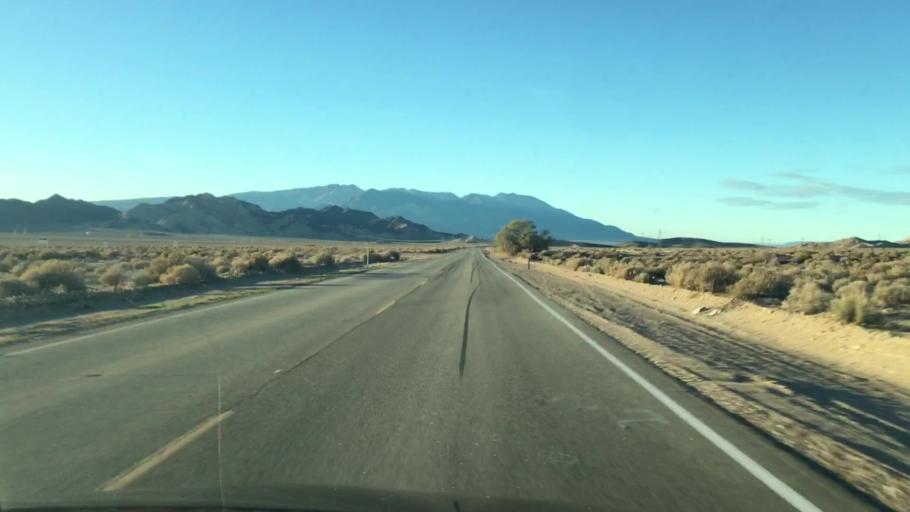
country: US
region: California
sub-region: San Bernardino County
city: Fort Irwin
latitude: 35.3697
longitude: -116.1145
